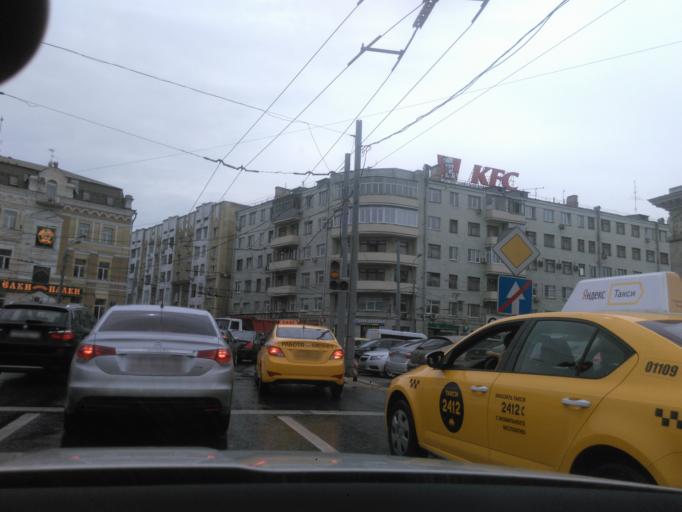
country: RU
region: Moskovskaya
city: Dorogomilovo
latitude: 55.7757
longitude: 37.5831
